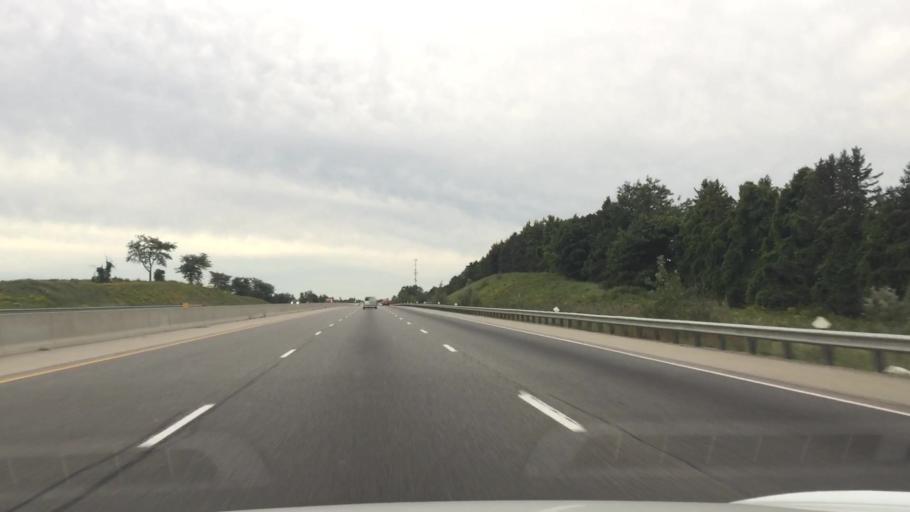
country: CA
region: Ontario
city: Kitchener
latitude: 43.2523
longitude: -80.5683
